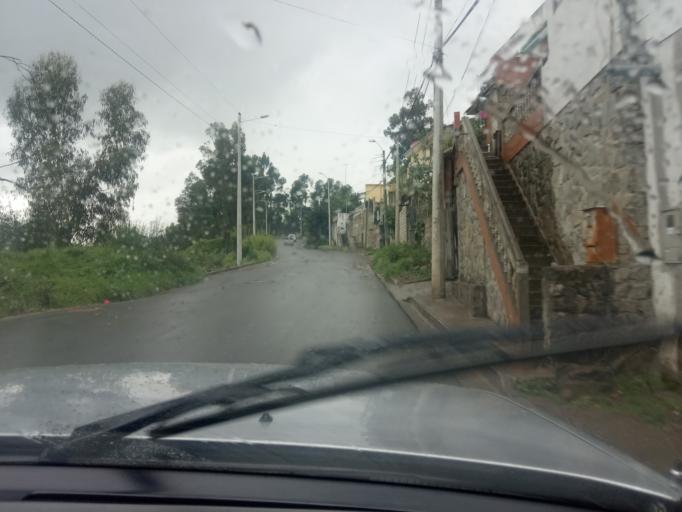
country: EC
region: Azuay
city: Llacao
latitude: -2.8634
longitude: -78.9400
